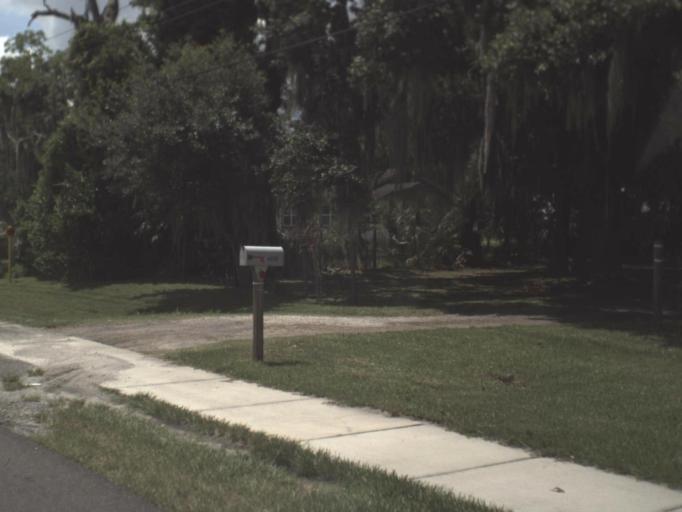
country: US
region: Florida
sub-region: Hillsborough County
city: Dover
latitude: 28.0051
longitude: -82.1775
